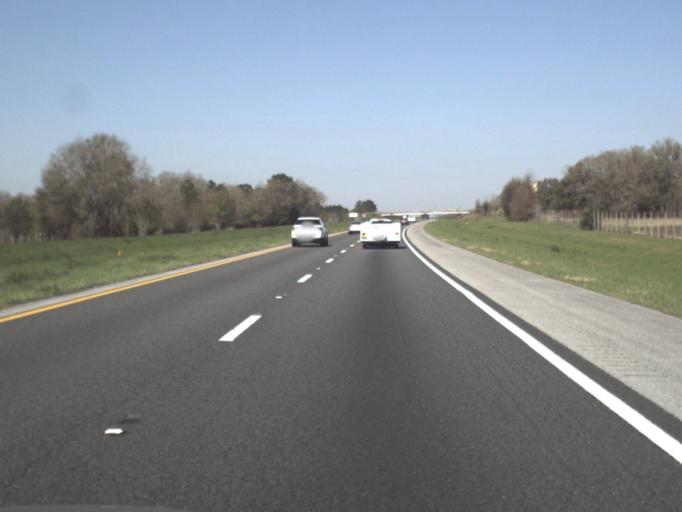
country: US
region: Florida
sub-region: Jackson County
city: Sneads
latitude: 30.6441
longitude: -85.0056
